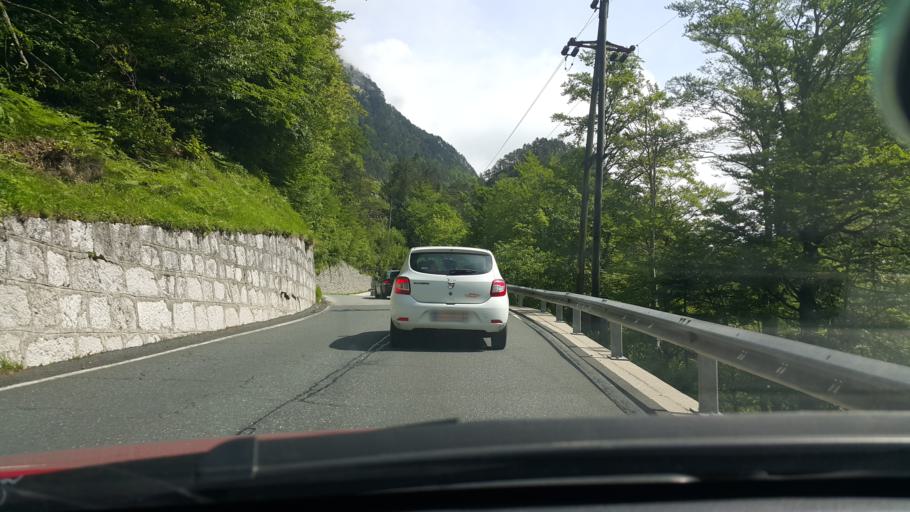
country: AT
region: Carinthia
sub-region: Politischer Bezirk Klagenfurt Land
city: Ferlach
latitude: 46.4830
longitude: 14.2614
